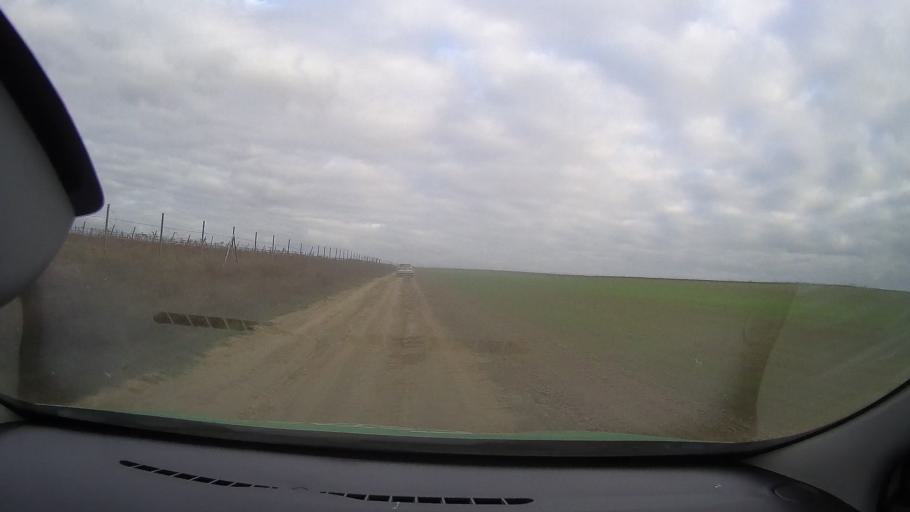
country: RO
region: Tulcea
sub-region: Comuna Jurilovca
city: Jurilovca
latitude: 44.7671
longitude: 28.9069
